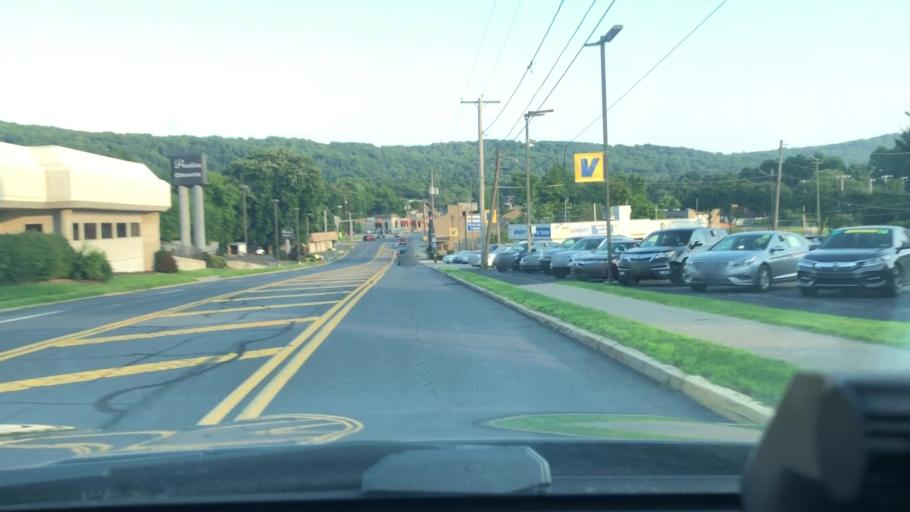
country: US
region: Pennsylvania
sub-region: Lehigh County
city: Emmaus
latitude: 40.5450
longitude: -75.4878
